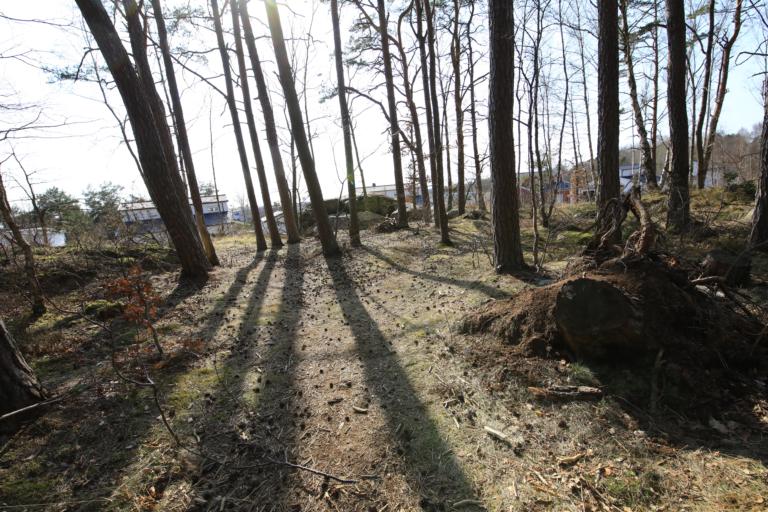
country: SE
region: Halland
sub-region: Varbergs Kommun
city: Varberg
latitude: 57.1460
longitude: 12.2816
